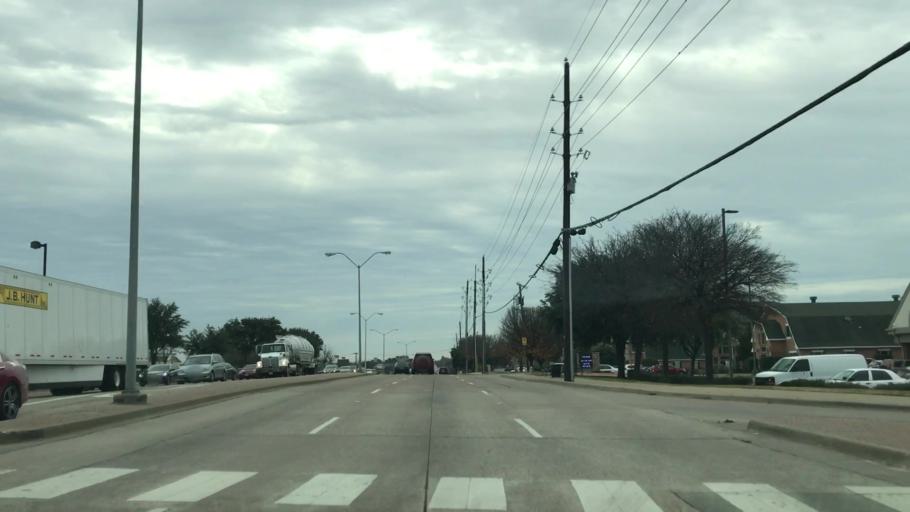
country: US
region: Texas
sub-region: Dallas County
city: Carrollton
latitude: 32.9733
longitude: -96.8900
